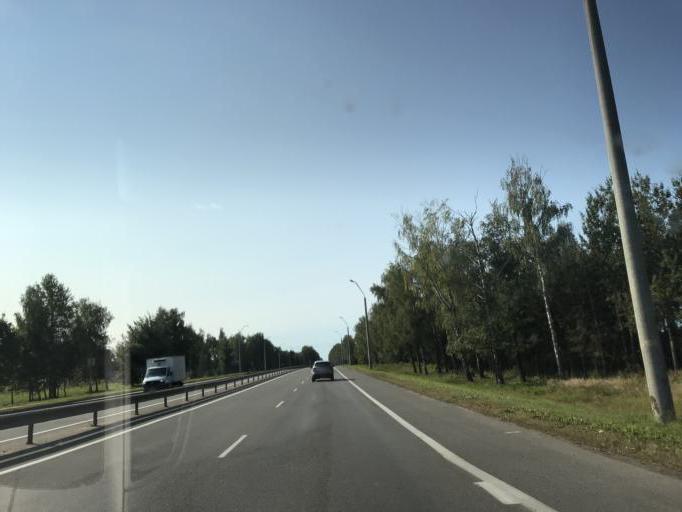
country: BY
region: Mogilev
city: Buynichy
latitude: 53.8536
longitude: 30.2544
